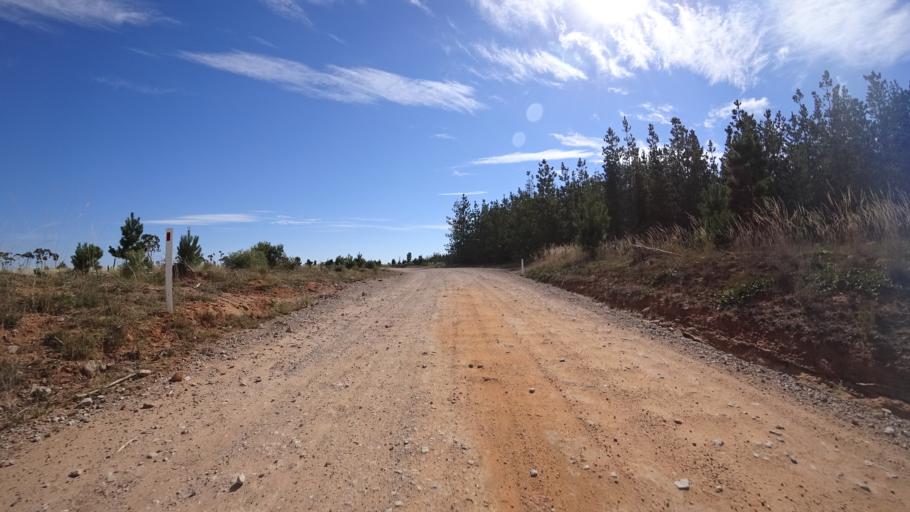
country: AU
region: New South Wales
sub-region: Lithgow
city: Lithgow
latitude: -33.3744
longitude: 150.2448
